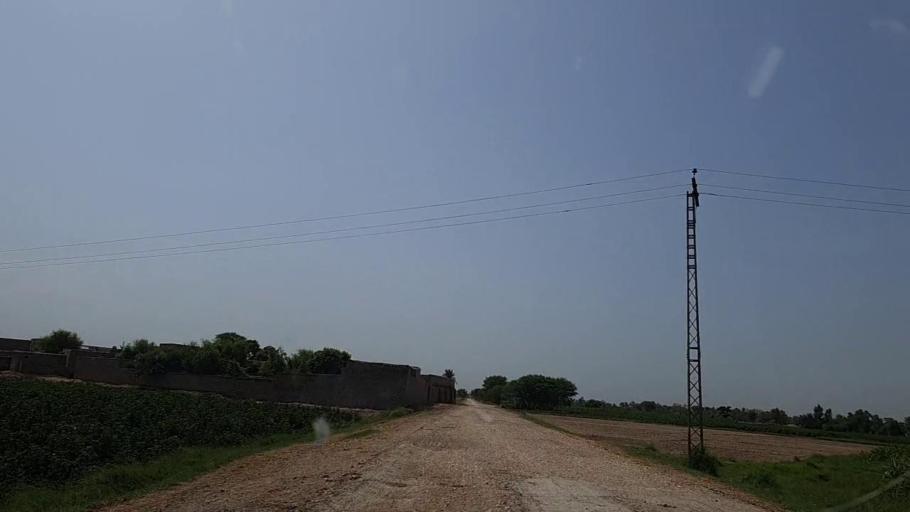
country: PK
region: Sindh
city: Naushahro Firoz
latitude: 26.8503
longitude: 68.0103
